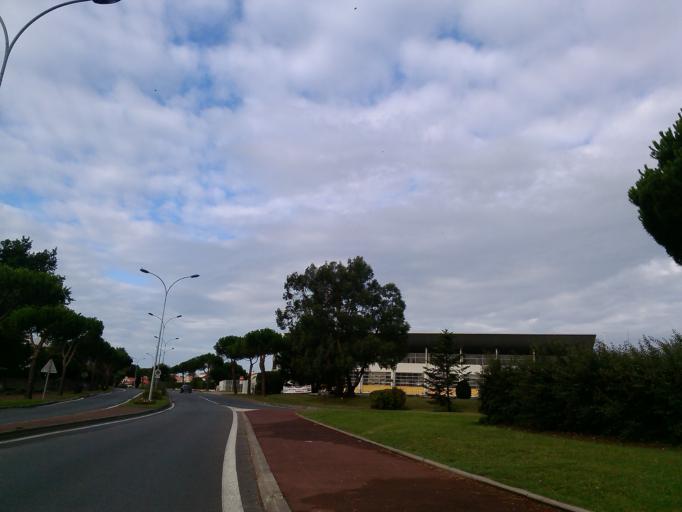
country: FR
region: Poitou-Charentes
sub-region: Departement de la Charente-Maritime
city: Royan
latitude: 45.6391
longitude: -1.0258
